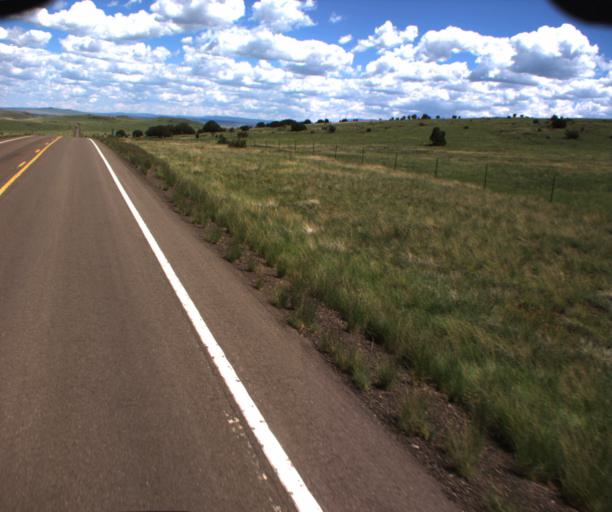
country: US
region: Arizona
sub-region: Apache County
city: Springerville
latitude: 34.2183
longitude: -109.4721
